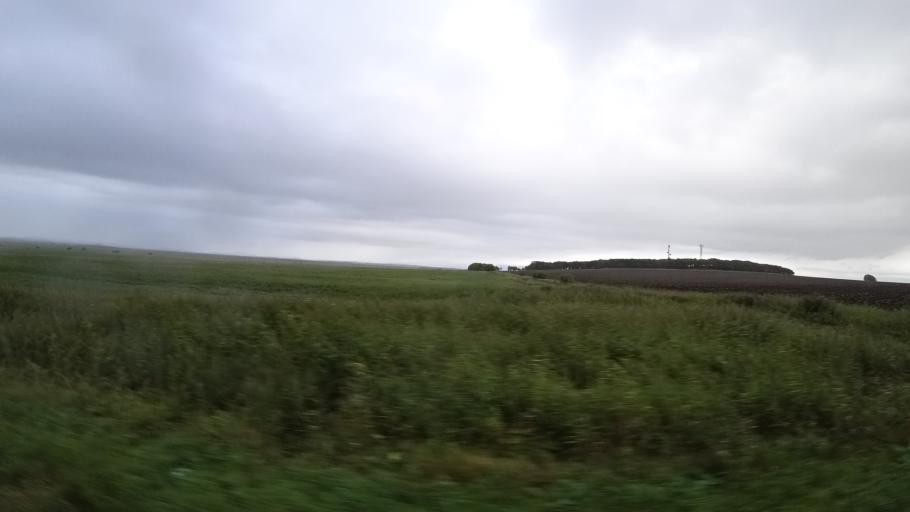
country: RU
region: Primorskiy
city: Chernigovka
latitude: 44.3728
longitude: 132.5298
